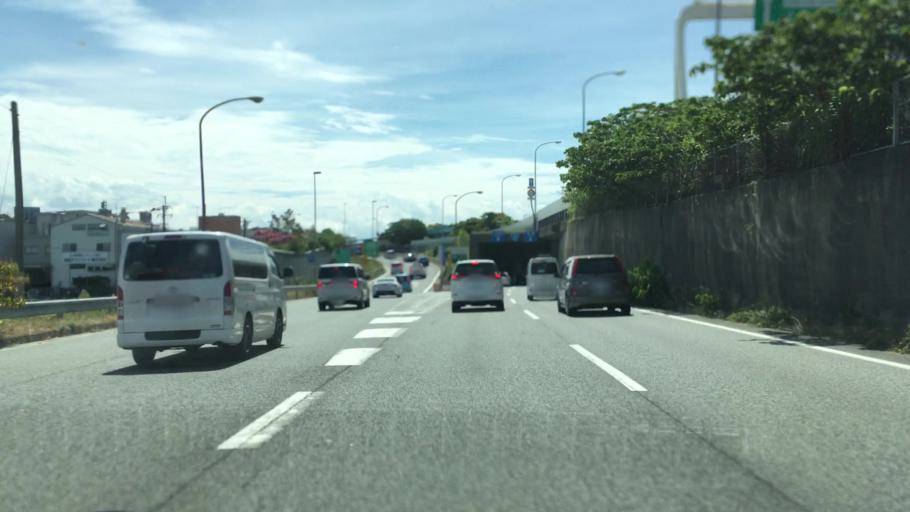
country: JP
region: Fukuoka
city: Onojo
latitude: 33.5331
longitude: 130.4903
